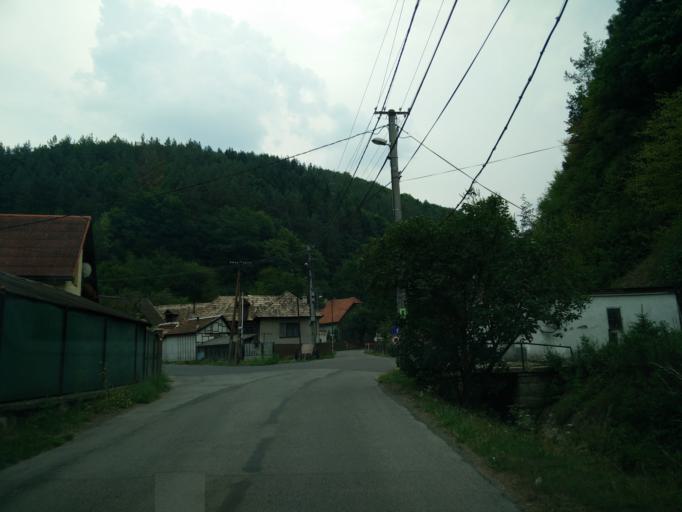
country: SK
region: Banskobystricky
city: Ziar nad Hronom
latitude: 48.5760
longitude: 18.8986
